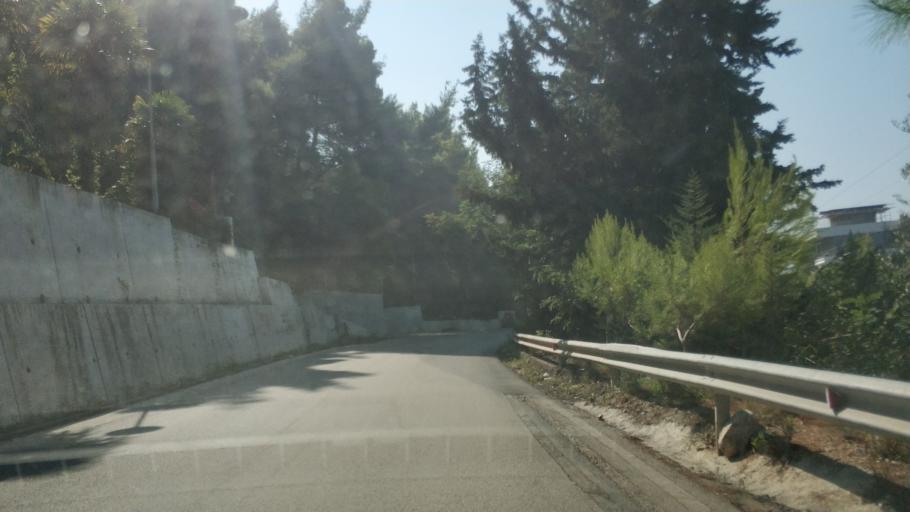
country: AL
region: Vlore
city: Vlore
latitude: 40.4048
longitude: 19.4802
